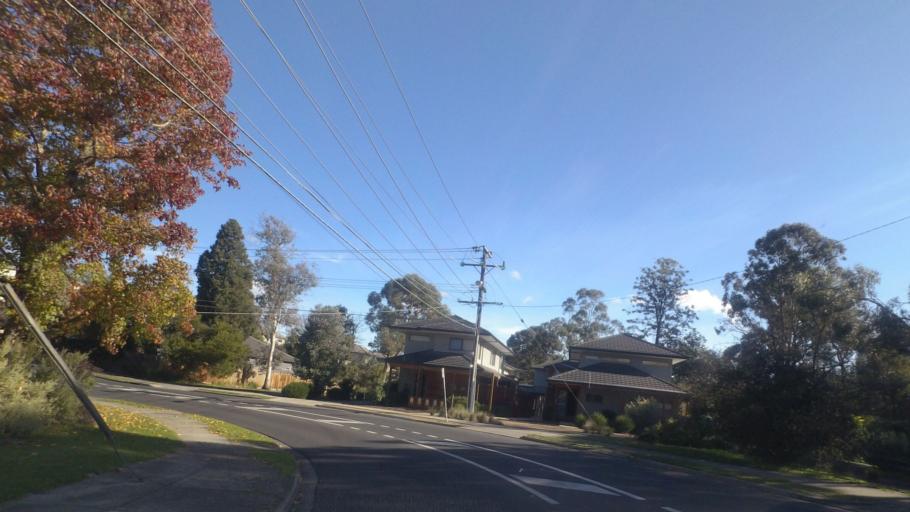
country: AU
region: Victoria
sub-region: Nillumbik
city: Eltham North
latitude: -37.7109
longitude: 145.1528
